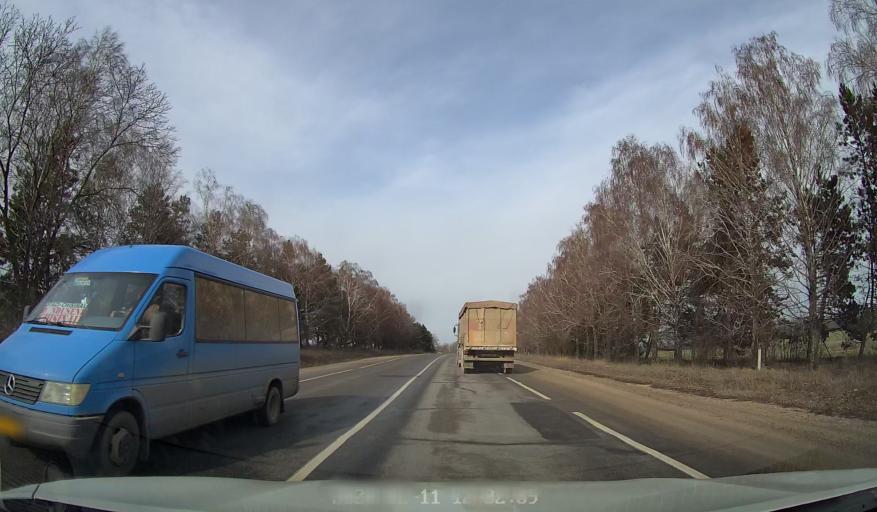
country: MD
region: Riscani
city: Riscani
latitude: 47.9475
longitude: 27.6241
